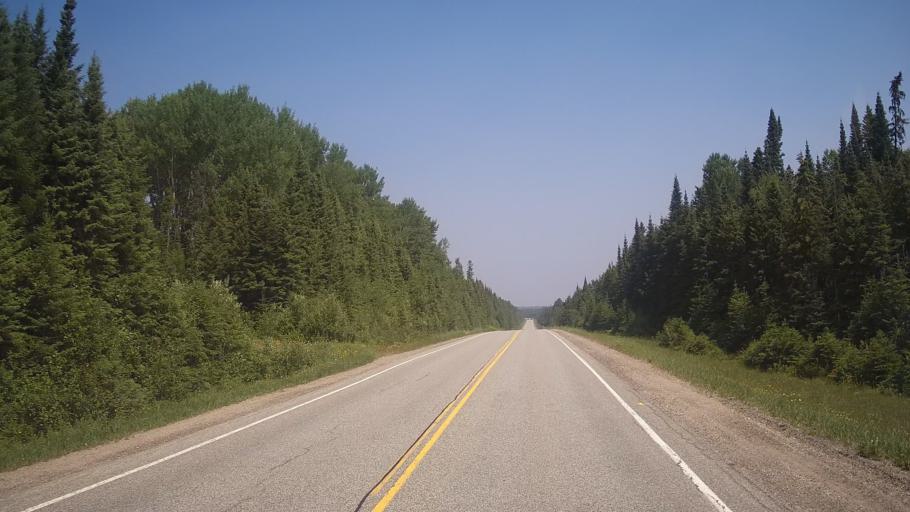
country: CA
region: Ontario
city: Timmins
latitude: 48.2022
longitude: -81.5786
